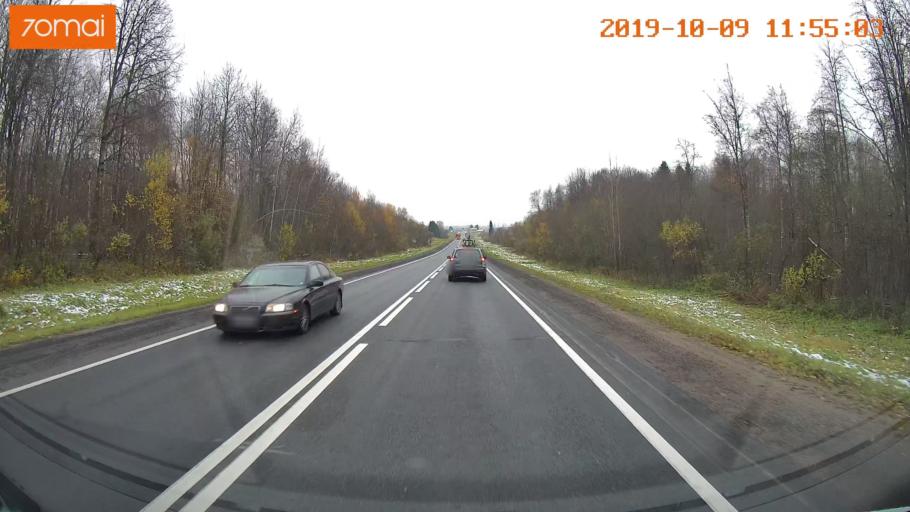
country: RU
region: Vologda
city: Gryazovets
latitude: 58.7520
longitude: 40.2843
